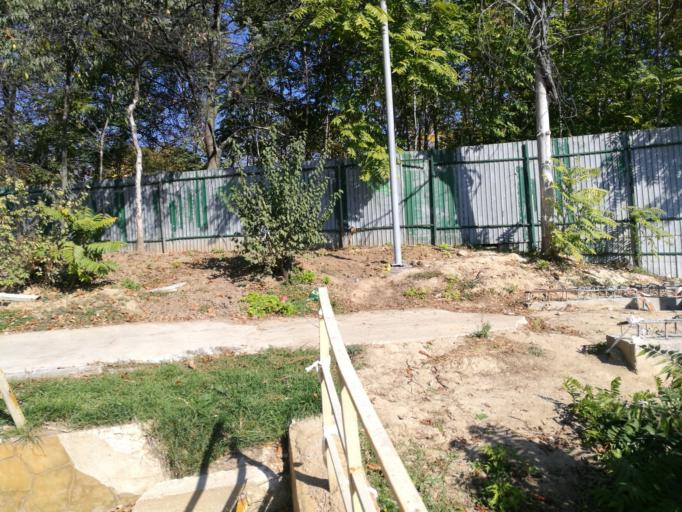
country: RO
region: Bucuresti
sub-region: Municipiul Bucuresti
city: Bucharest
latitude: 44.4731
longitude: 26.0905
